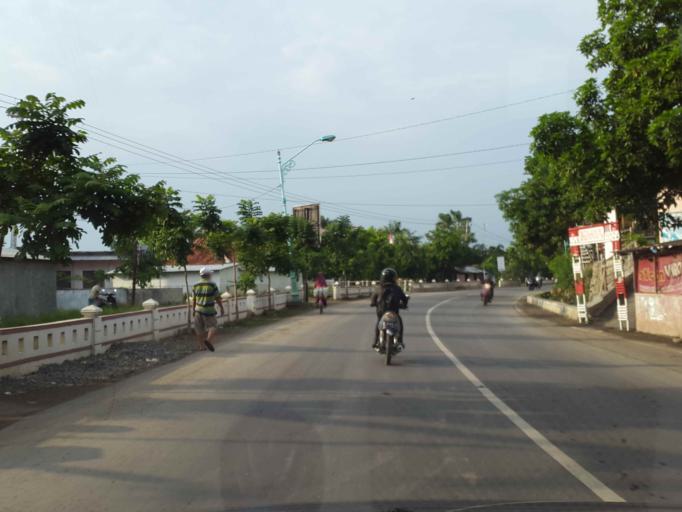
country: ID
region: Central Java
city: Dukuhturi
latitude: -6.8795
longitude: 109.0391
